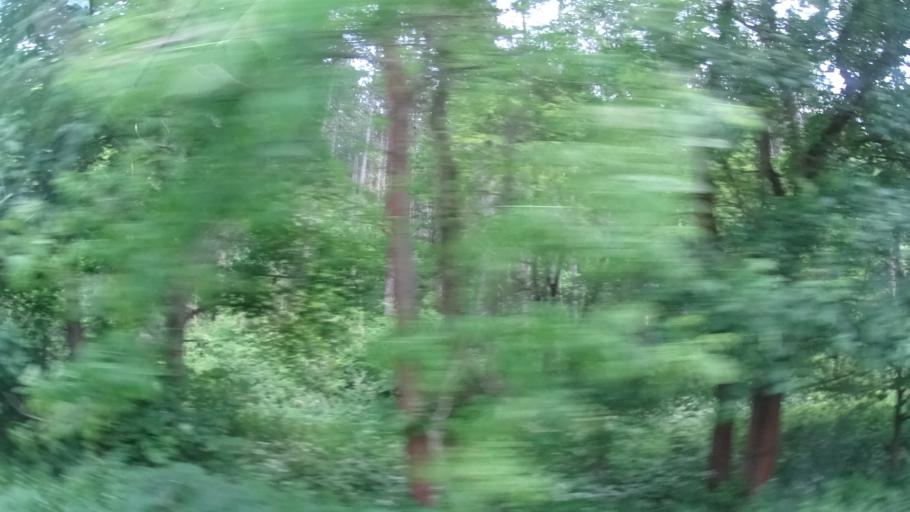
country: DE
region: Thuringia
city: Plaue
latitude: 50.8214
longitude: 10.9112
